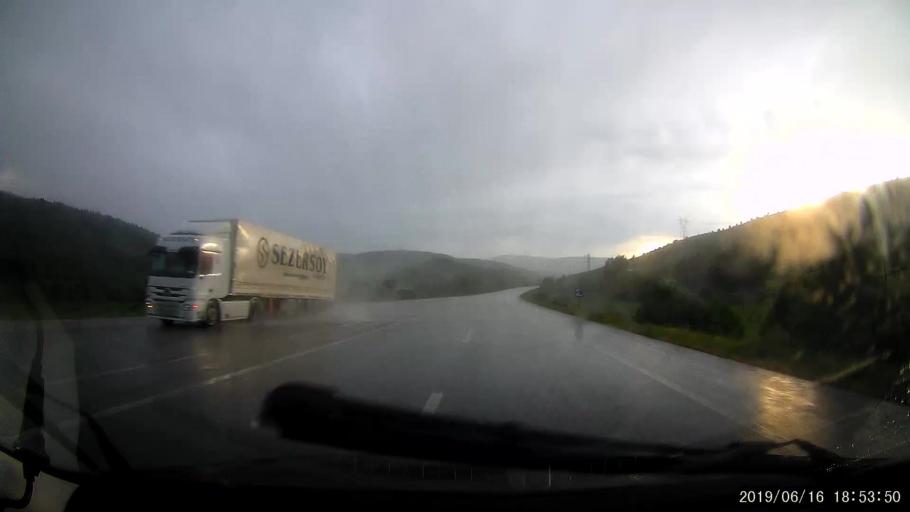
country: TR
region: Erzincan
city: Catalcam
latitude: 39.8969
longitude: 38.8680
